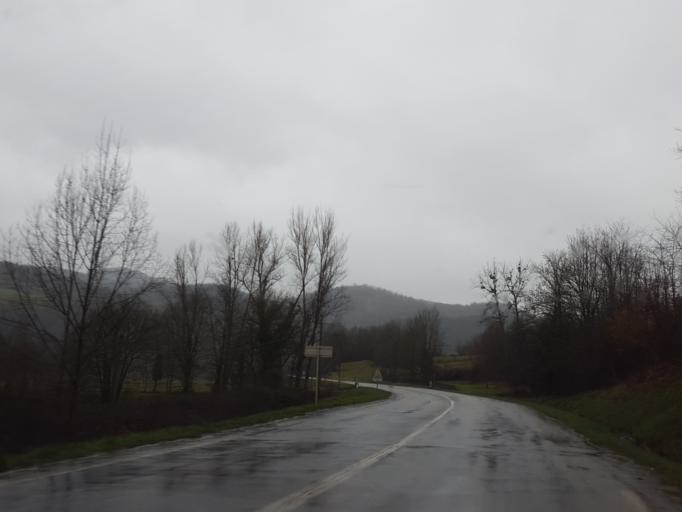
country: FR
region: Midi-Pyrenees
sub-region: Departement de l'Ariege
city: Montjoie-en-Couserans
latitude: 43.0152
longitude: 1.3692
